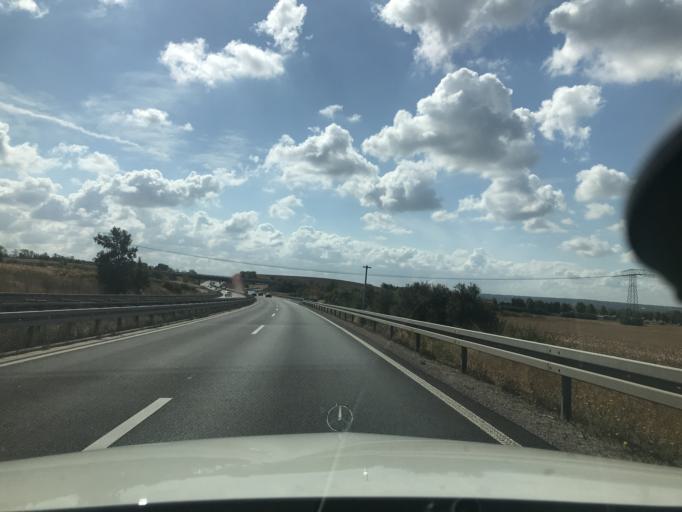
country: DE
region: Thuringia
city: Erfurt
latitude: 51.0173
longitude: 11.0577
